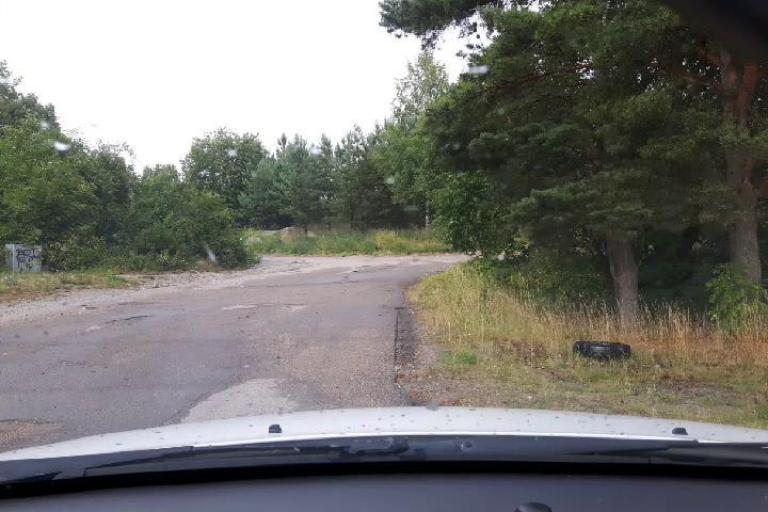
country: SE
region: Uppsala
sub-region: Uppsala Kommun
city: Gamla Uppsala
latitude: 59.9066
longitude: 17.6094
